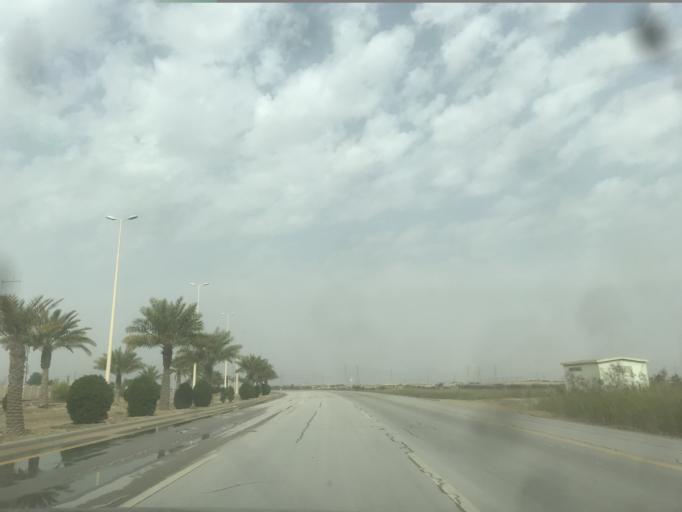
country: SA
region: Eastern Province
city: Dhahran
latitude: 26.1997
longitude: 50.0423
